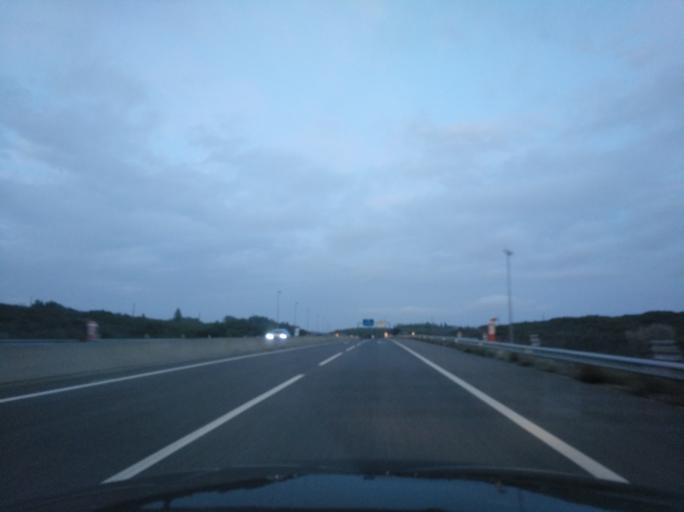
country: PT
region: Faro
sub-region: Lagos
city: Lagos
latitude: 37.1530
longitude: -8.6973
